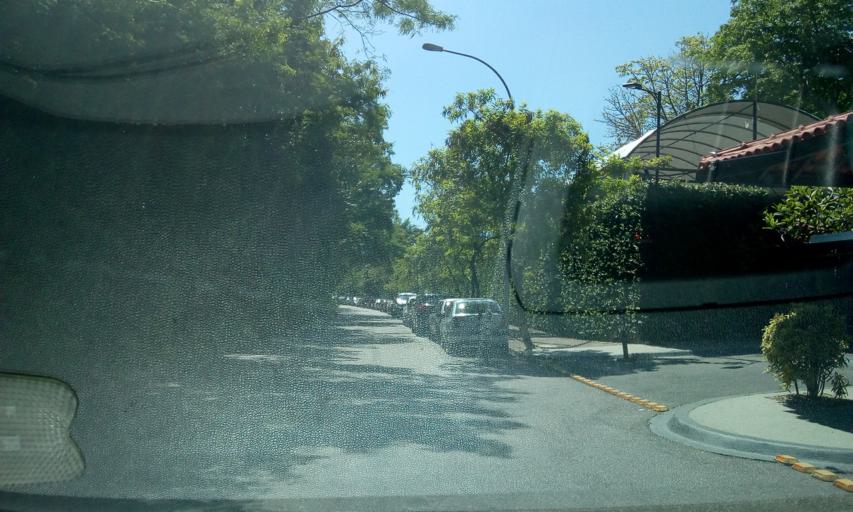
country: BR
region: Rio de Janeiro
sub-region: Rio De Janeiro
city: Rio de Janeiro
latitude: -23.0084
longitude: -43.3233
